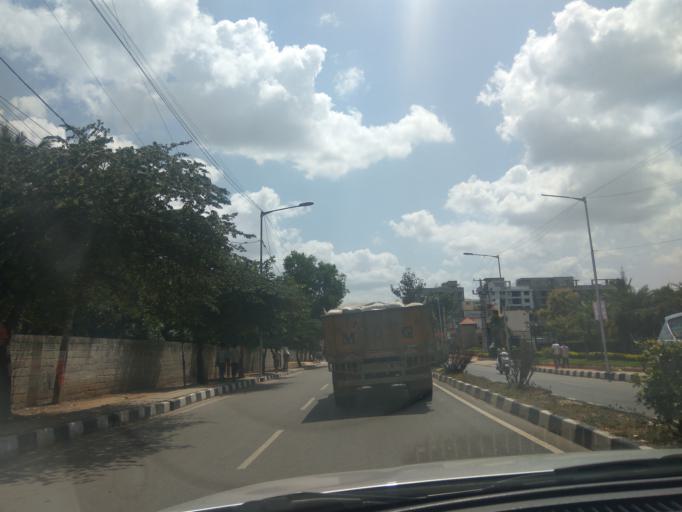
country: IN
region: Karnataka
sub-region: Bangalore Urban
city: Yelahanka
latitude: 13.1215
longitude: 77.6212
